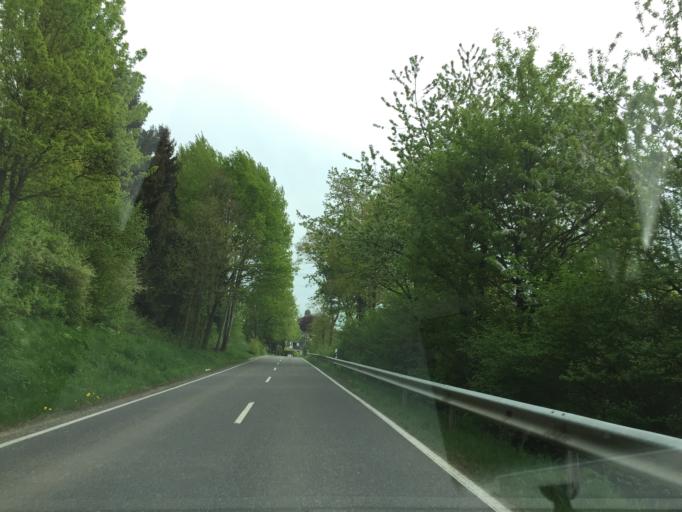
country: DE
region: Rheinland-Pfalz
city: Steinefrenz
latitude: 50.4639
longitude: 7.9345
